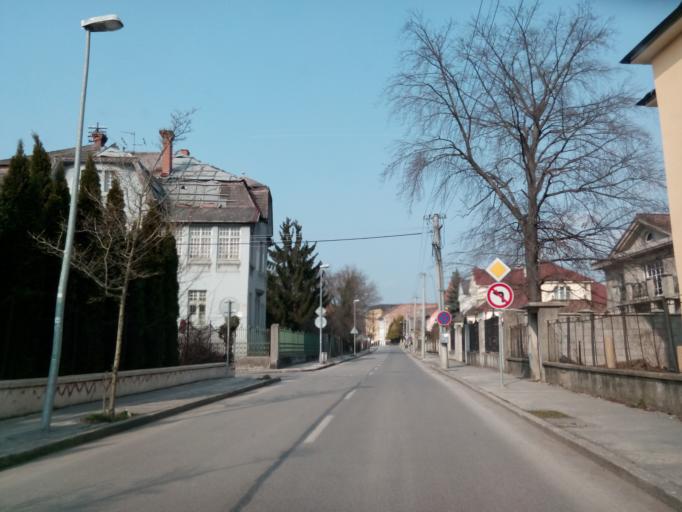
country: SK
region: Trenciansky
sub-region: Okres Trencin
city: Trencin
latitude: 48.8901
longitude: 18.0335
